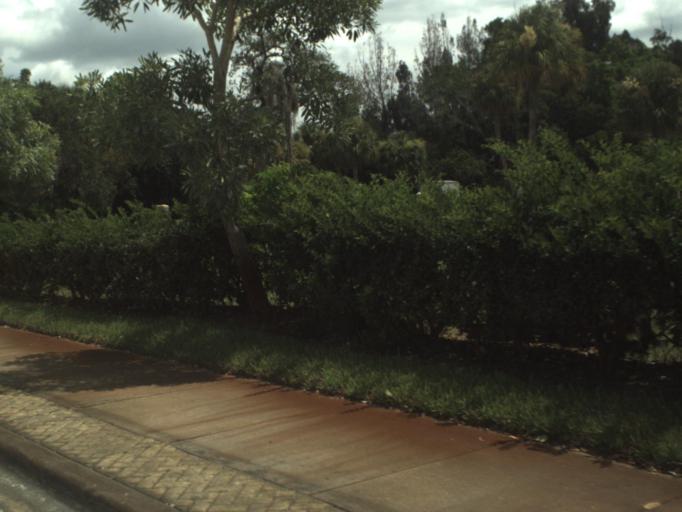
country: US
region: Florida
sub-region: Martin County
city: Stuart
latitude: 27.1865
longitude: -80.2530
